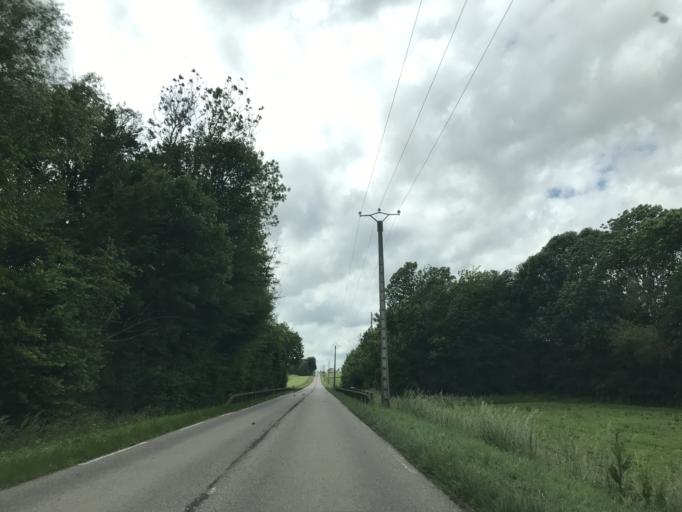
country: FR
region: Ile-de-France
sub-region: Departement des Yvelines
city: Breval
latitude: 48.9591
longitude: 1.5230
